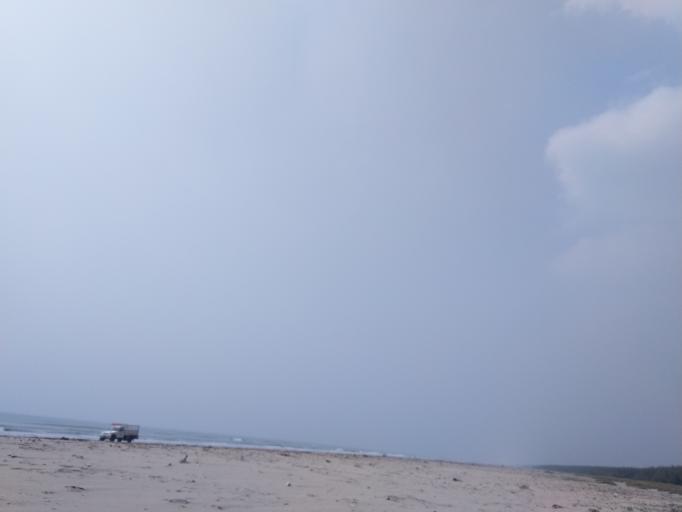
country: IN
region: Andhra Pradesh
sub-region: Krishna
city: Kanuru
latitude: 16.3483
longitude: 81.4362
